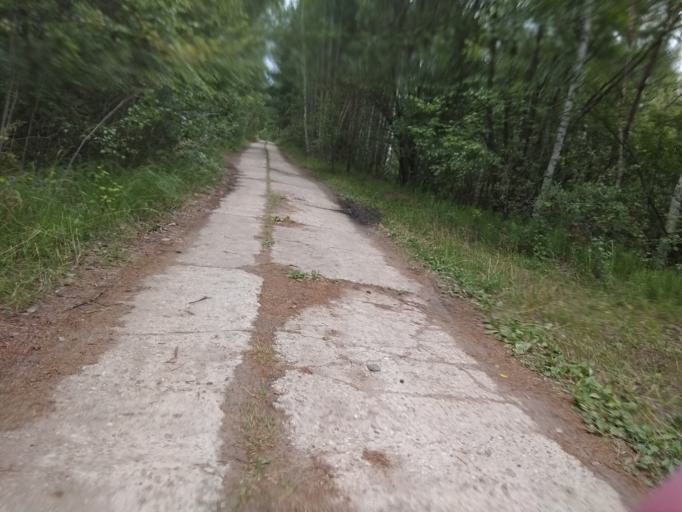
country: RU
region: Moskovskaya
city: Misheronskiy
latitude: 55.6214
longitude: 39.7147
